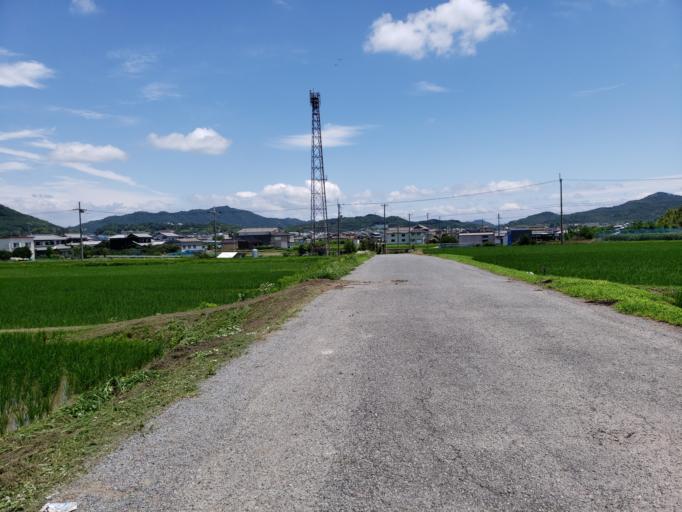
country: JP
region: Hyogo
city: Kakogawacho-honmachi
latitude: 34.8156
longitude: 134.8119
